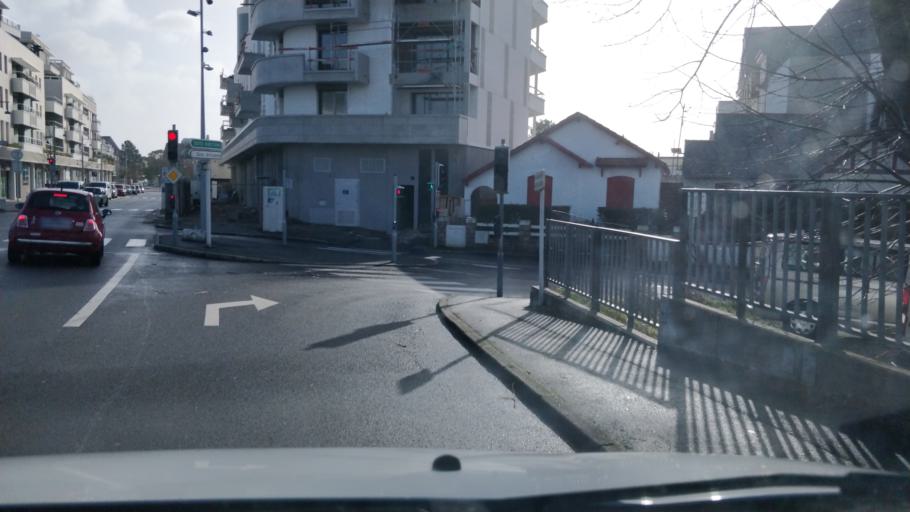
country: FR
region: Pays de la Loire
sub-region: Departement de la Loire-Atlantique
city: La Baule-Escoublac
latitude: 47.2878
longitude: -2.3931
